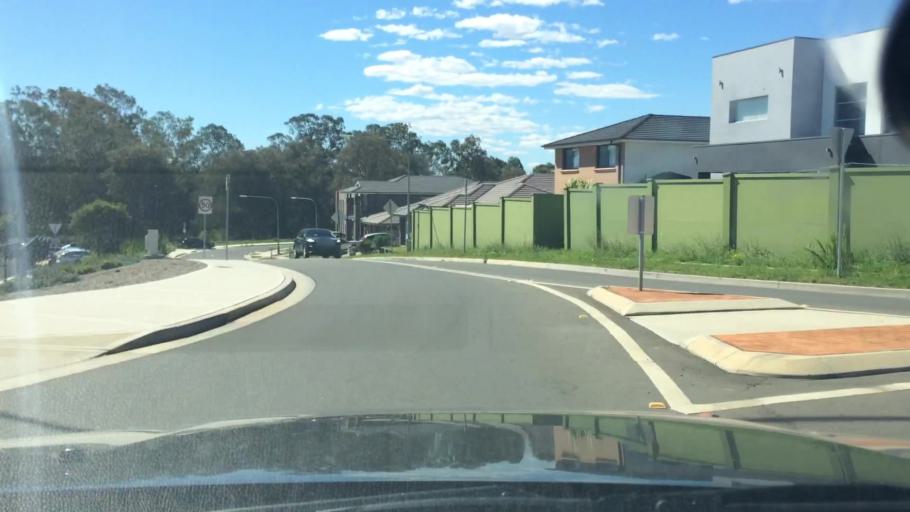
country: AU
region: New South Wales
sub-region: Liverpool
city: Miller
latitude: -33.9360
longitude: 150.8469
